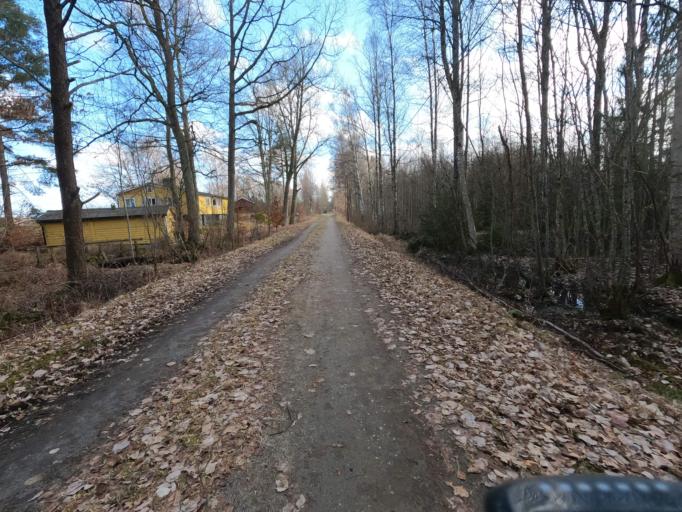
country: SE
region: Kronoberg
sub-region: Vaxjo Kommun
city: Gemla
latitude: 56.6880
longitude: 14.6076
